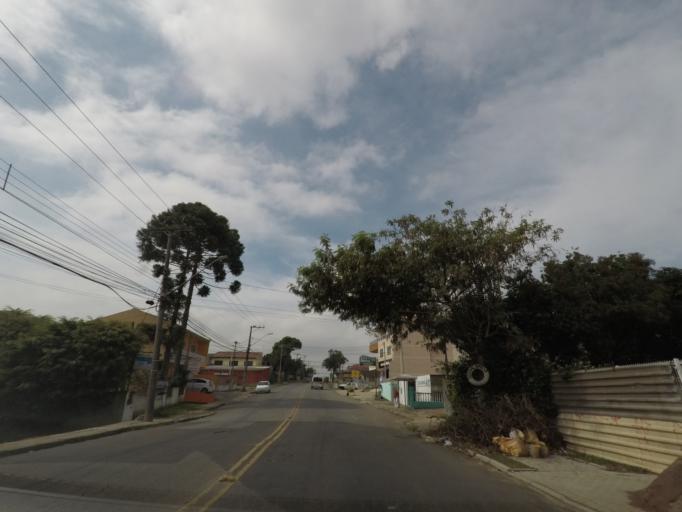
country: BR
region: Parana
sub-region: Curitiba
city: Curitiba
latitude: -25.4891
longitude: -49.3072
